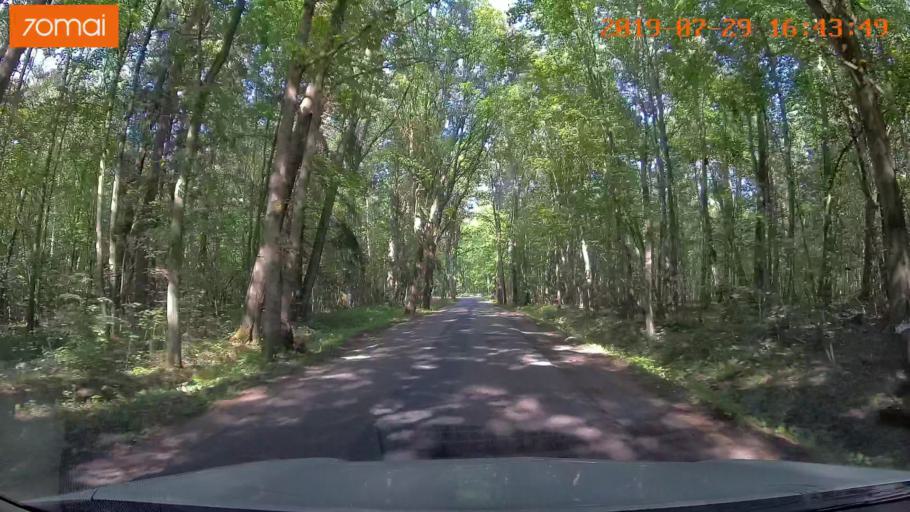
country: RU
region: Kaliningrad
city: Primorsk
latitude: 54.7511
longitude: 20.0887
